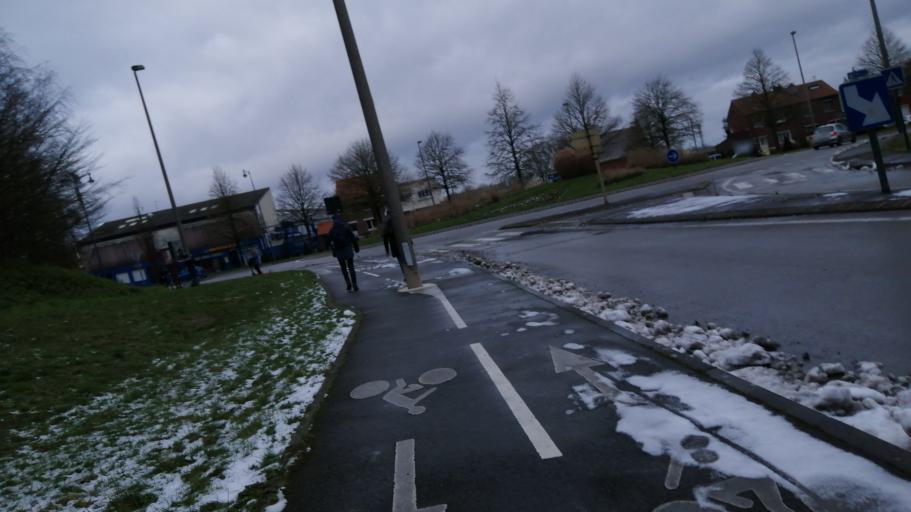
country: FR
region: Nord-Pas-de-Calais
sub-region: Departement du Pas-de-Calais
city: Saint-Laurent-Blangy
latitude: 50.2820
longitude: 2.8028
